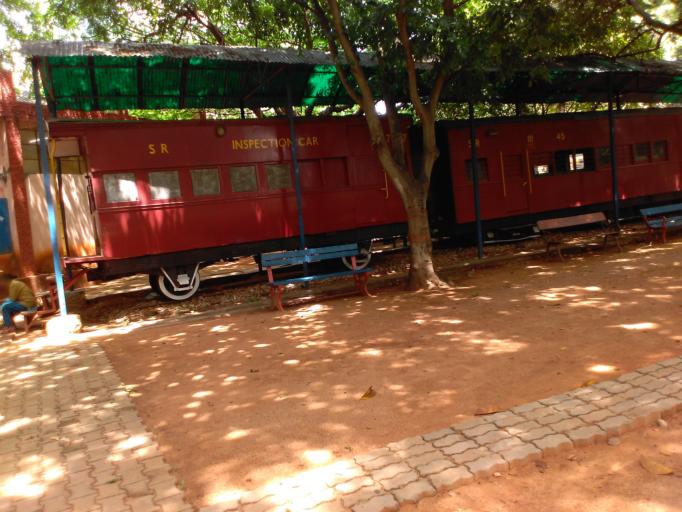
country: IN
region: Karnataka
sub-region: Mysore
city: Mysore
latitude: 12.3136
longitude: 76.6451
